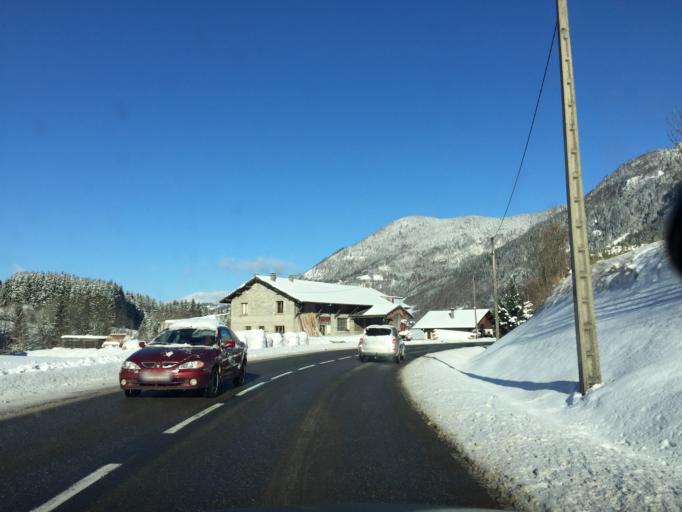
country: FR
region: Rhone-Alpes
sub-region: Departement de la Haute-Savoie
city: Abondance
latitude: 46.3175
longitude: 6.6743
